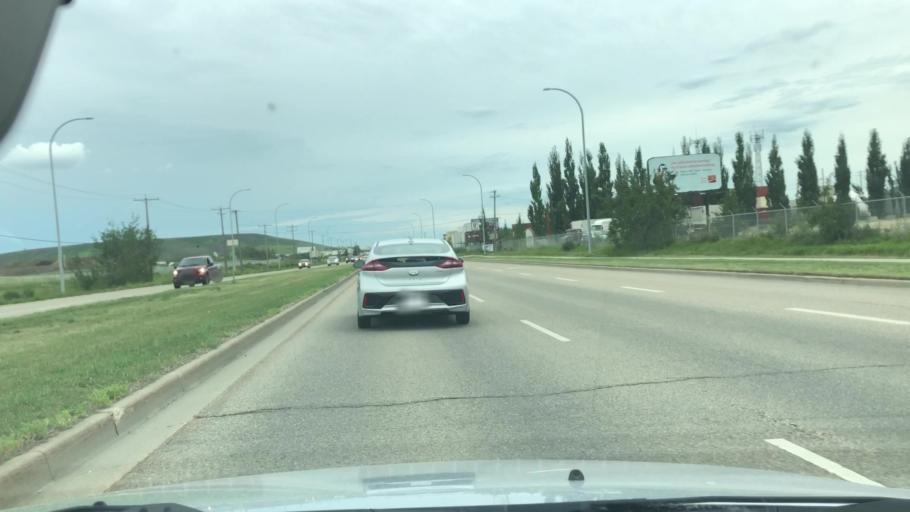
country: CA
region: Alberta
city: St. Albert
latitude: 53.5979
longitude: -113.6152
